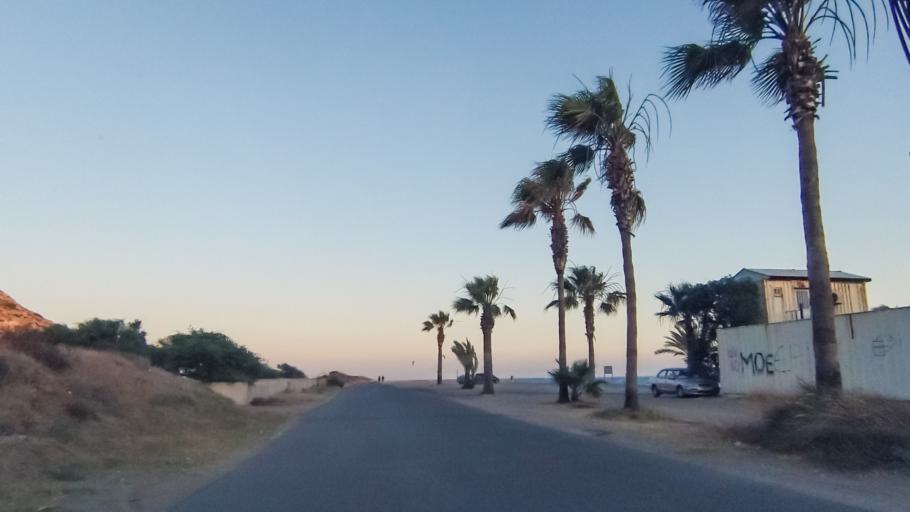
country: CY
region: Limassol
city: Erimi
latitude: 34.6632
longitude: 32.8820
